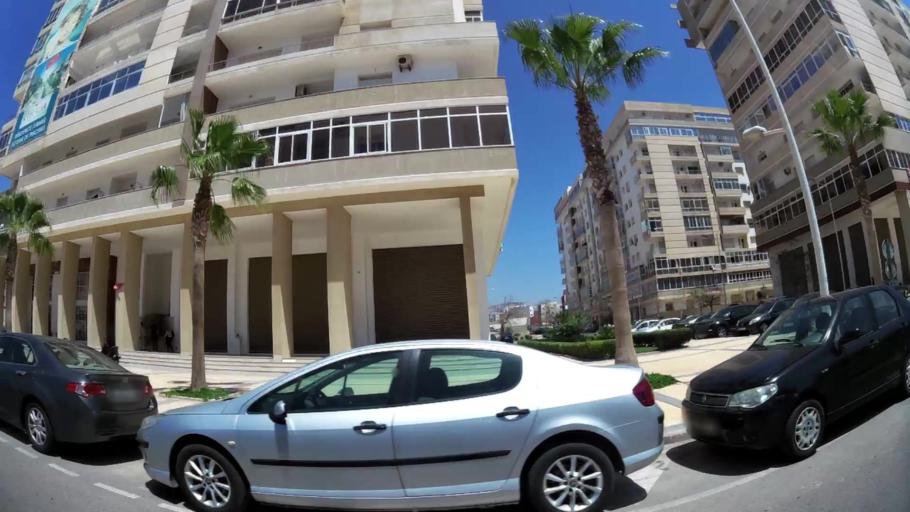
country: MA
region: Oued ed Dahab-Lagouira
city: Dakhla
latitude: 30.4379
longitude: -9.5642
